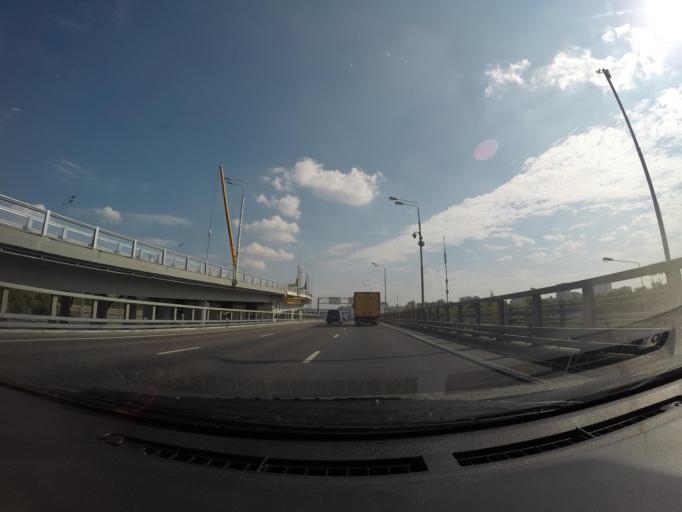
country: RU
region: Moscow
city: Likhobory
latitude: 55.8510
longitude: 37.5487
